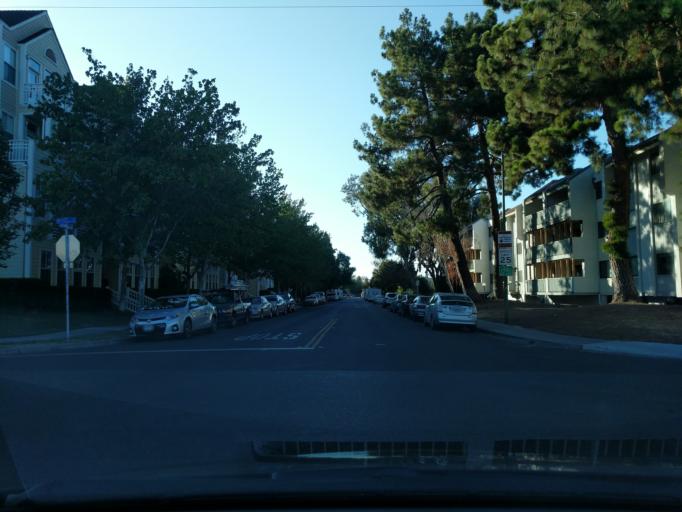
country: US
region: California
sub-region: Santa Clara County
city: Los Altos
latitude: 37.3991
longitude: -122.1054
